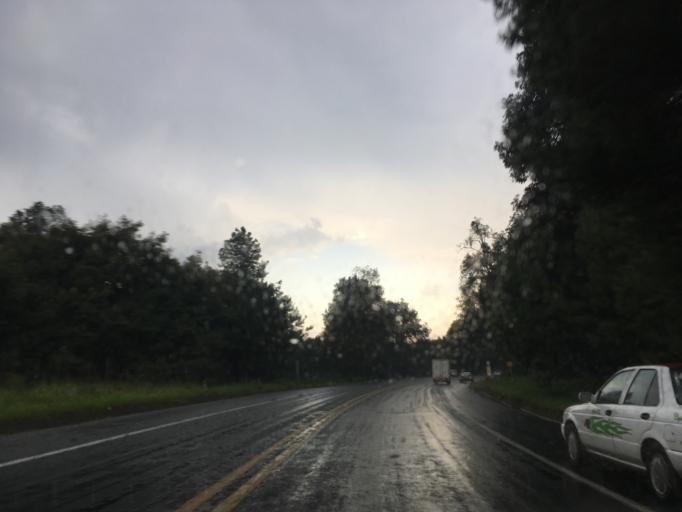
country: MX
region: Michoacan
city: Capacuaro
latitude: 19.5258
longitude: -102.0765
